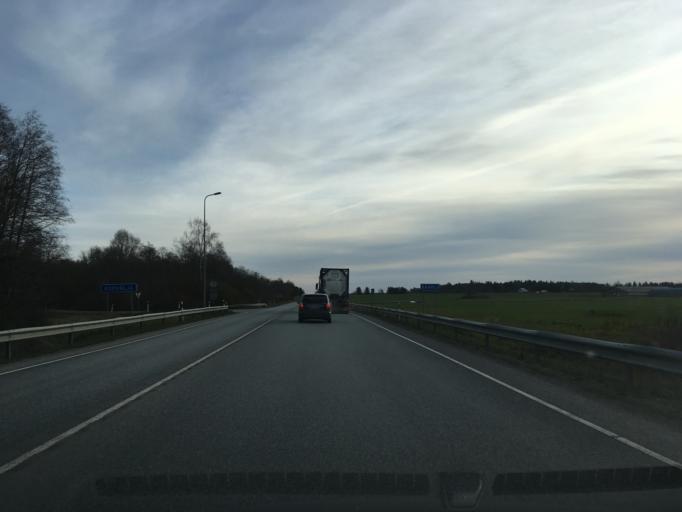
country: EE
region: Laeaene-Virumaa
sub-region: Someru vald
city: Someru
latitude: 59.3649
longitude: 26.4406
